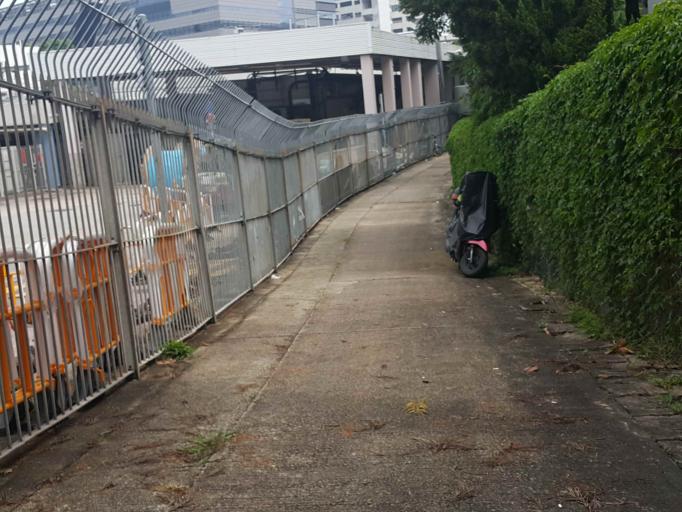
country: HK
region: Wong Tai Sin
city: Wong Tai Sin
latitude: 22.3380
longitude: 114.1749
